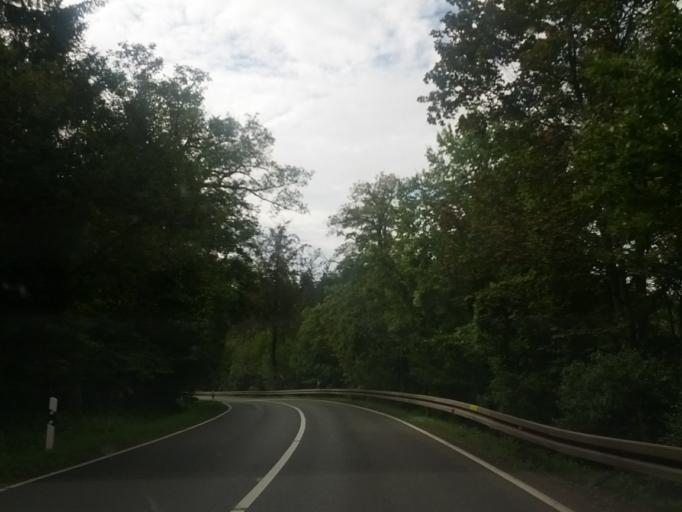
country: DE
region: Thuringia
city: Wolfsburg-Unkeroda
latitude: 50.8737
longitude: 10.2854
